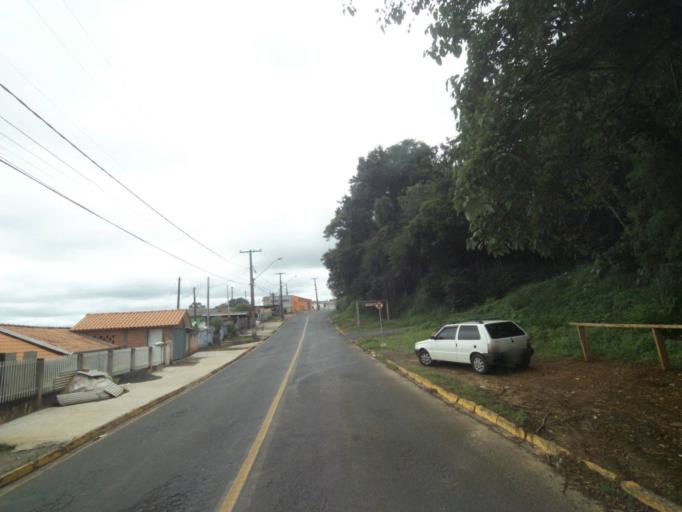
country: BR
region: Parana
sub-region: Telemaco Borba
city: Telemaco Borba
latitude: -24.3157
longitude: -50.6171
